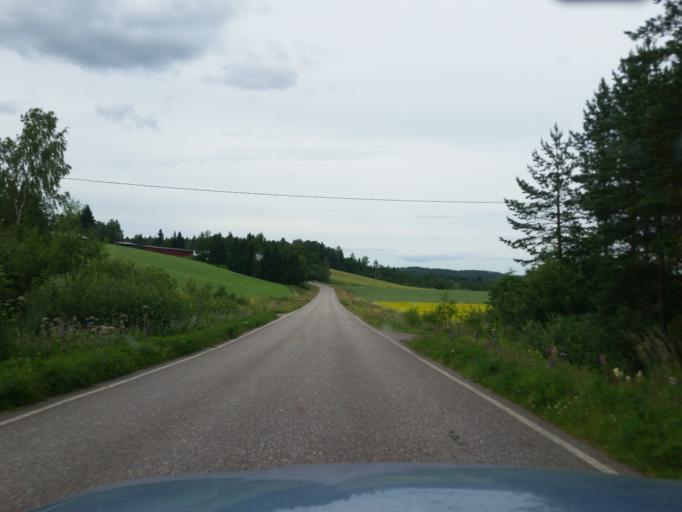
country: FI
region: Uusimaa
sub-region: Helsinki
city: Sammatti
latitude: 60.4133
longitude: 23.8250
